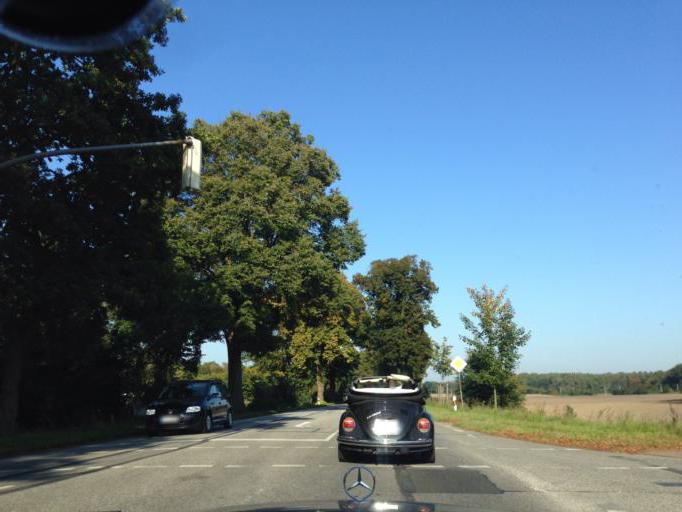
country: DE
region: Schleswig-Holstein
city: Ahrensburg
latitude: 53.6456
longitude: 10.2013
